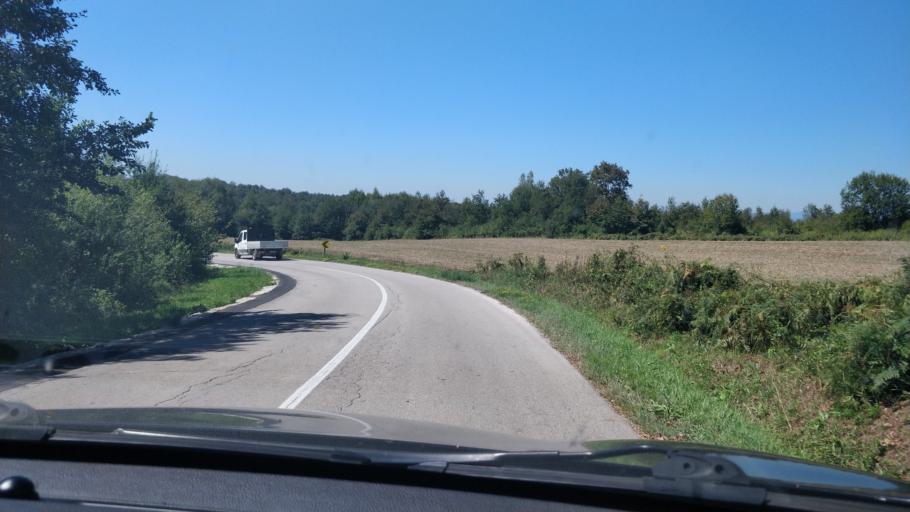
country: HR
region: Karlovacka
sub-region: Grad Karlovac
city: Karlovac
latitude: 45.4675
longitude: 15.6348
